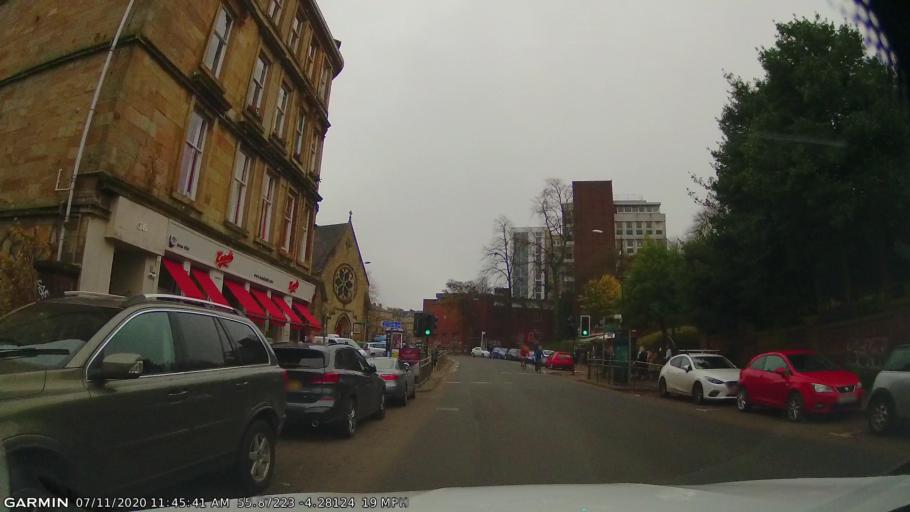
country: GB
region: Scotland
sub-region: Glasgow City
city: Glasgow
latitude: 55.8723
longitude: -4.2815
